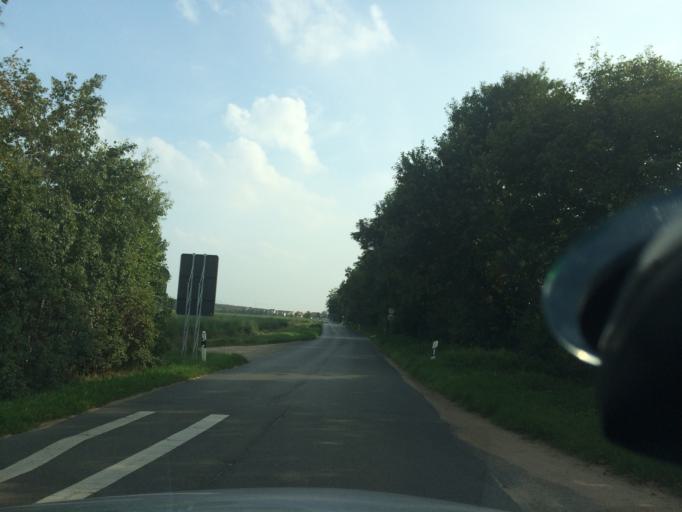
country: DE
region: Hesse
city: Griesheim
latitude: 49.8783
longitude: 8.5643
